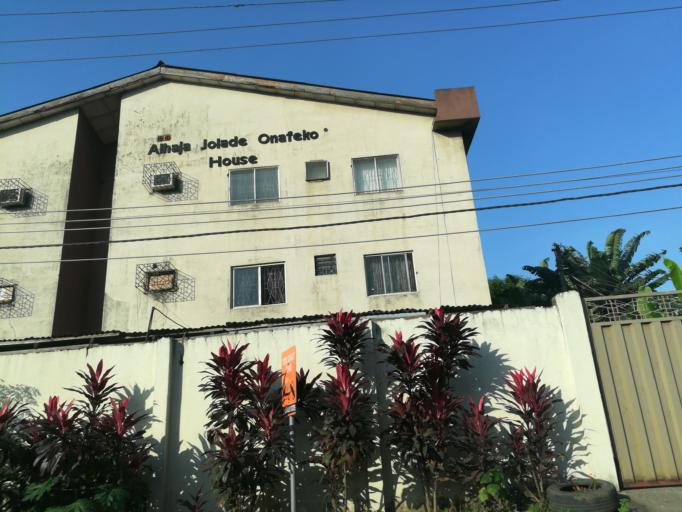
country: NG
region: Lagos
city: Ojota
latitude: 6.5858
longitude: 3.3656
